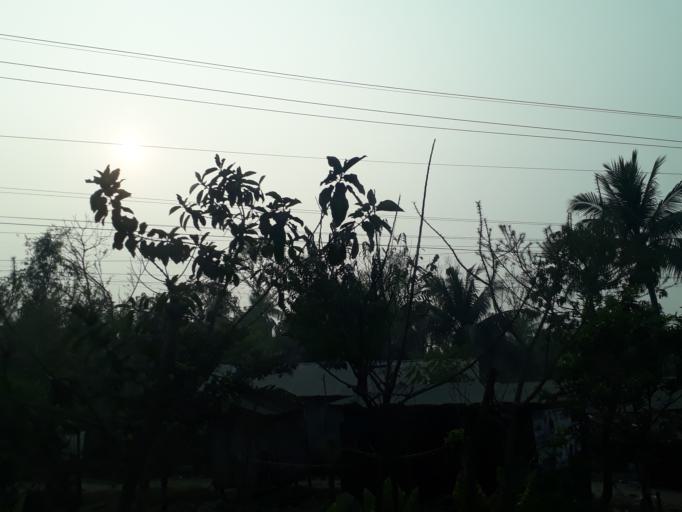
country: BD
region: Khulna
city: Bhatpara Abhaynagar
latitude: 22.9369
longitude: 89.4872
